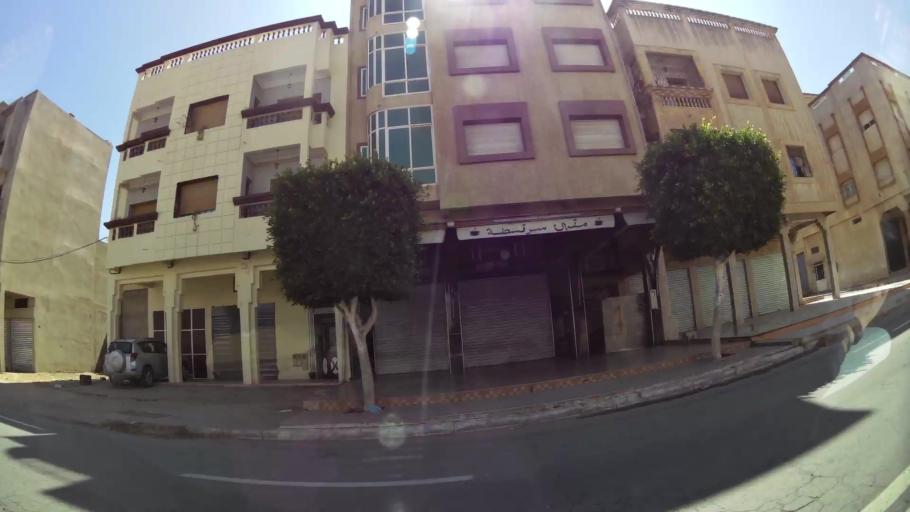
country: MA
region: Gharb-Chrarda-Beni Hssen
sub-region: Kenitra Province
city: Kenitra
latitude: 34.2386
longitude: -6.5461
